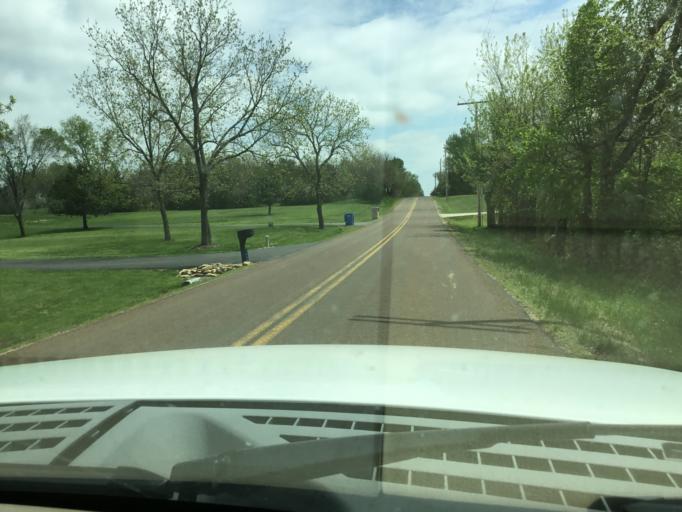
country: US
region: Kansas
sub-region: Shawnee County
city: Auburn
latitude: 38.9708
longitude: -95.7876
